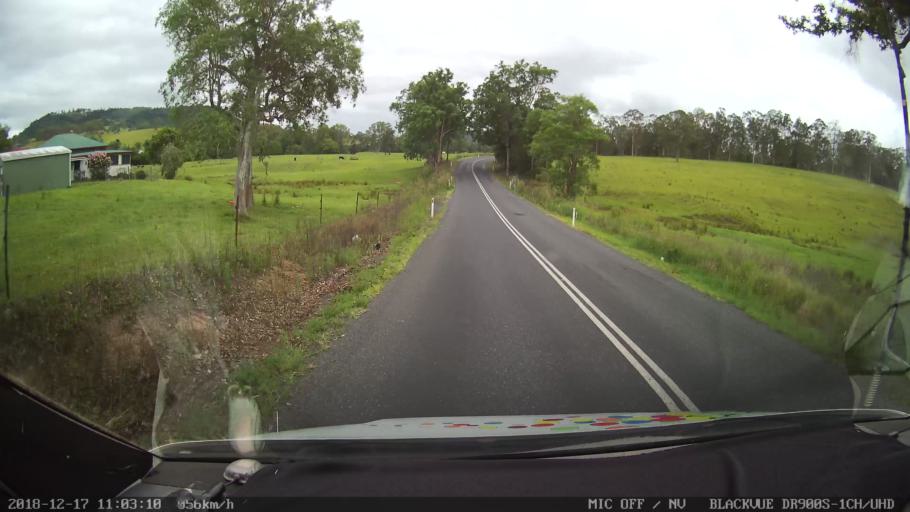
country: AU
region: New South Wales
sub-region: Kyogle
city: Kyogle
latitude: -28.8085
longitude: 152.6362
